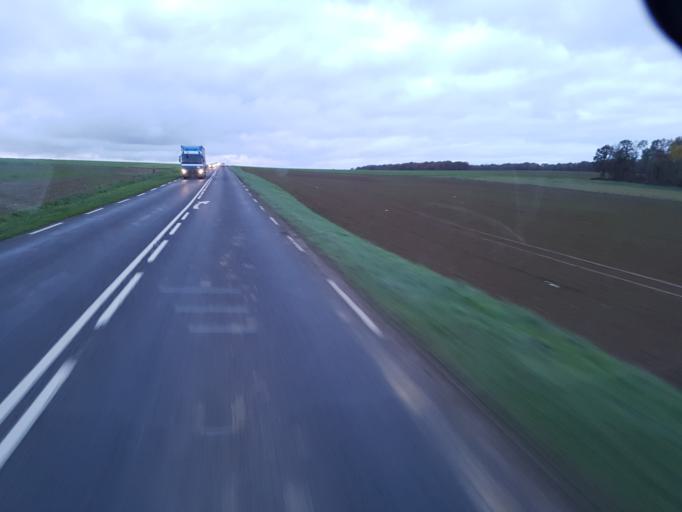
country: FR
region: Picardie
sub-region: Departement de l'Aisne
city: Coincy
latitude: 49.1153
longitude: 3.3953
